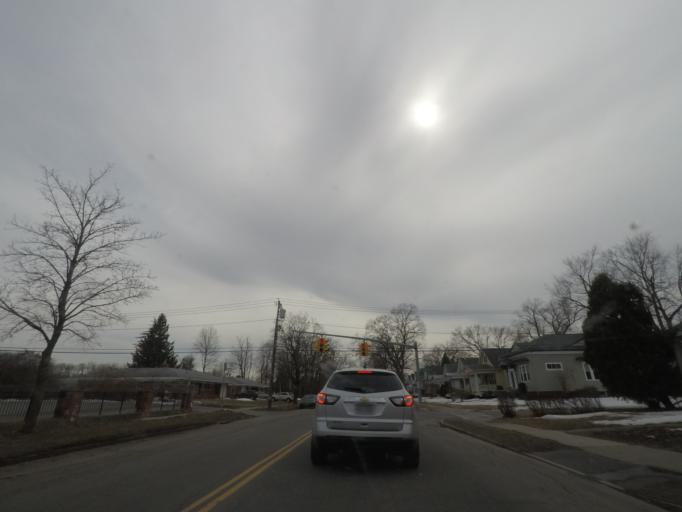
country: US
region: New York
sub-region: Albany County
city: Albany
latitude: 42.6508
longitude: -73.7852
